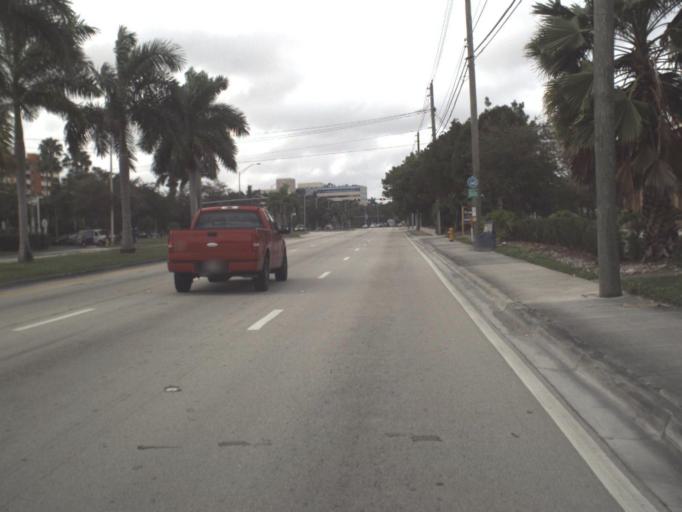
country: US
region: Florida
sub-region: Miami-Dade County
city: Doral
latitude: 25.8100
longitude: -80.3325
